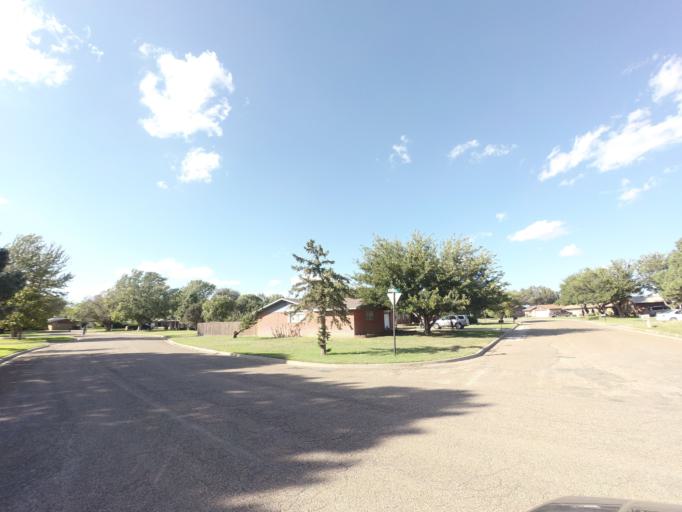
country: US
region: New Mexico
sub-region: Curry County
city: Clovis
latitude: 34.4359
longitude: -103.1830
